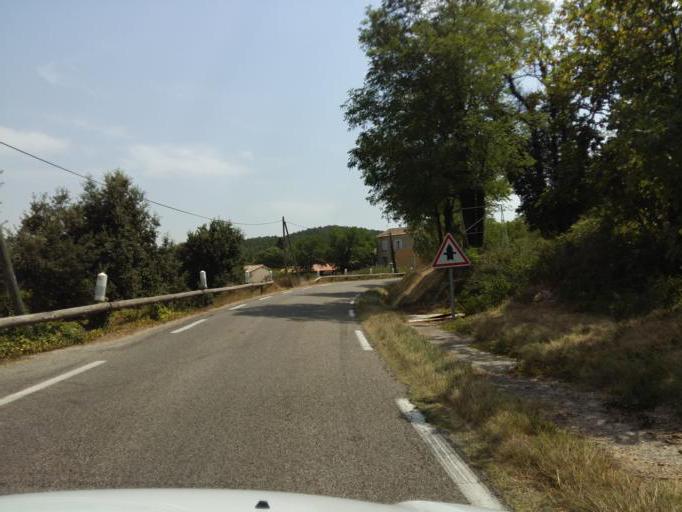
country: FR
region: Rhone-Alpes
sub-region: Departement de la Drome
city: Rochegude
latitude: 44.2586
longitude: 4.7914
